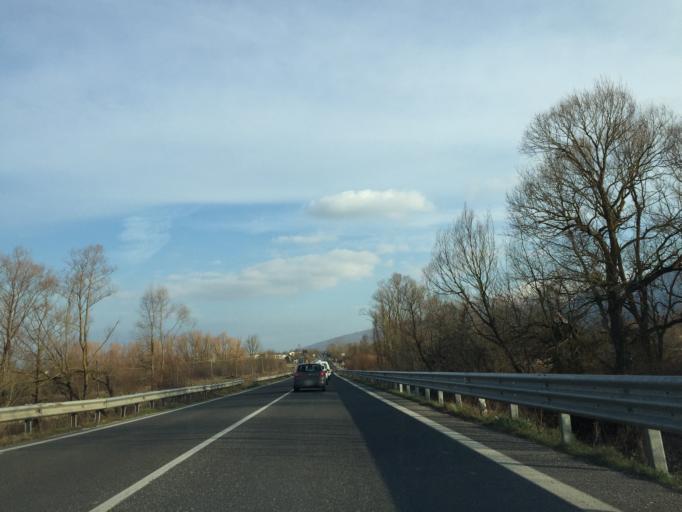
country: IT
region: Molise
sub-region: Provincia di Campobasso
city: Bojano
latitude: 41.4837
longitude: 14.4931
